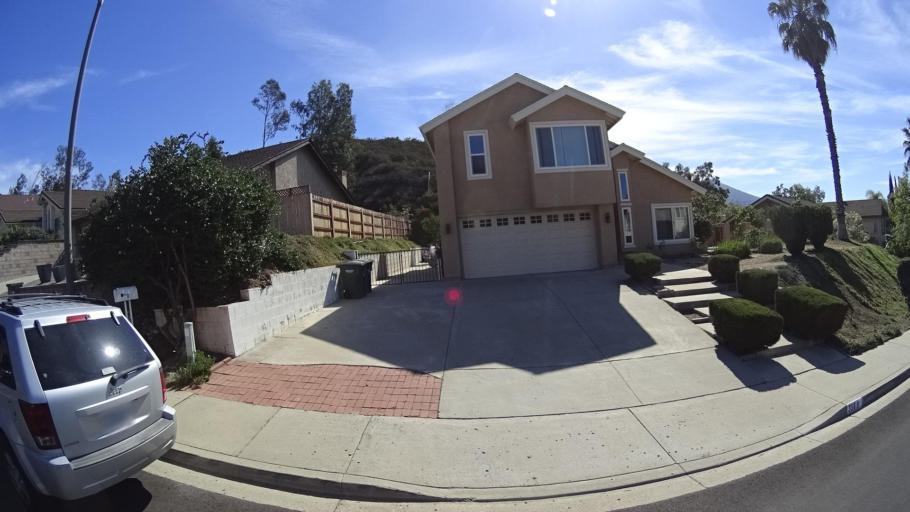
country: US
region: California
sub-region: San Diego County
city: Rancho San Diego
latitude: 32.7466
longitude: -116.9530
